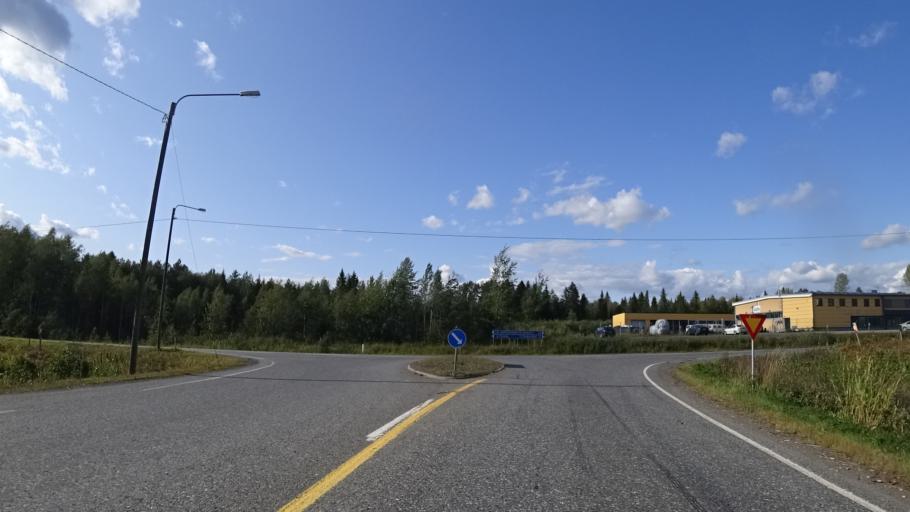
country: FI
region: North Karelia
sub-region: Keski-Karjala
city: Kitee
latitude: 62.0973
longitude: 30.1110
